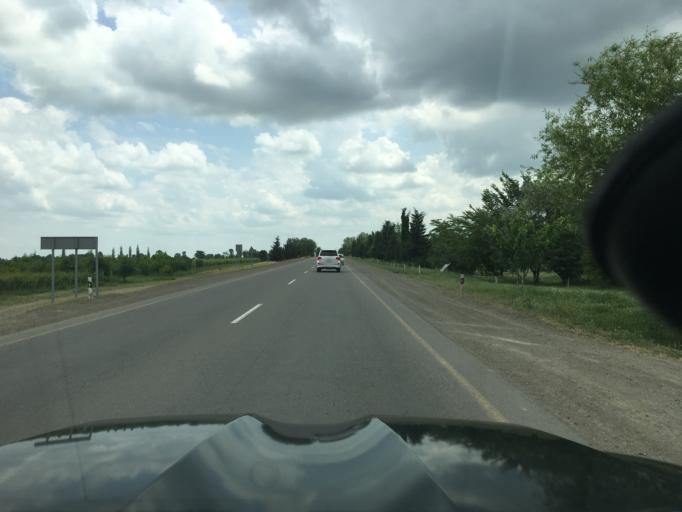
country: AZ
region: Tovuz
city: Tovuz
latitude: 40.9700
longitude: 45.6913
